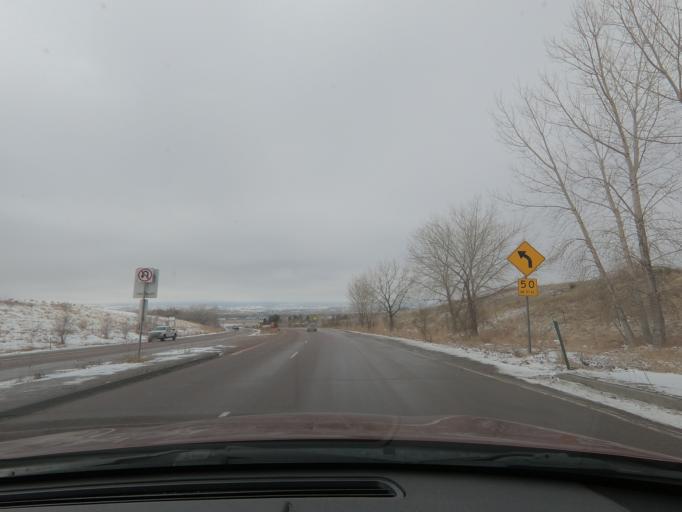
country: US
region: Colorado
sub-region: El Paso County
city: Security-Widefield
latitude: 38.7199
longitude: -104.7031
